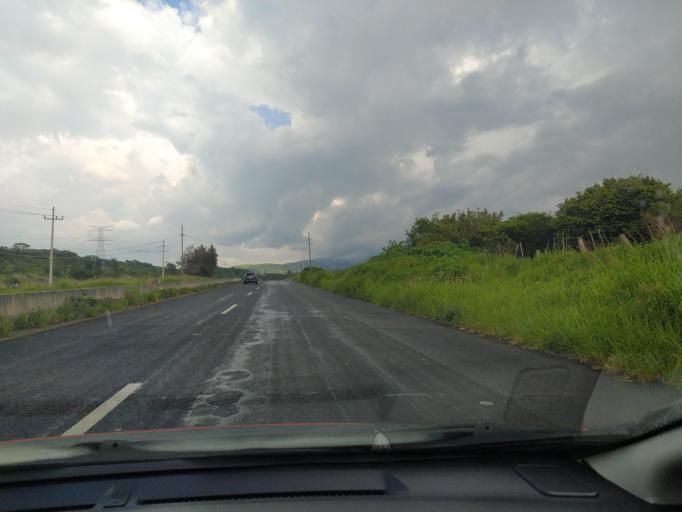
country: MX
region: Jalisco
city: Bellavista
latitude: 20.4334
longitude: -103.5956
